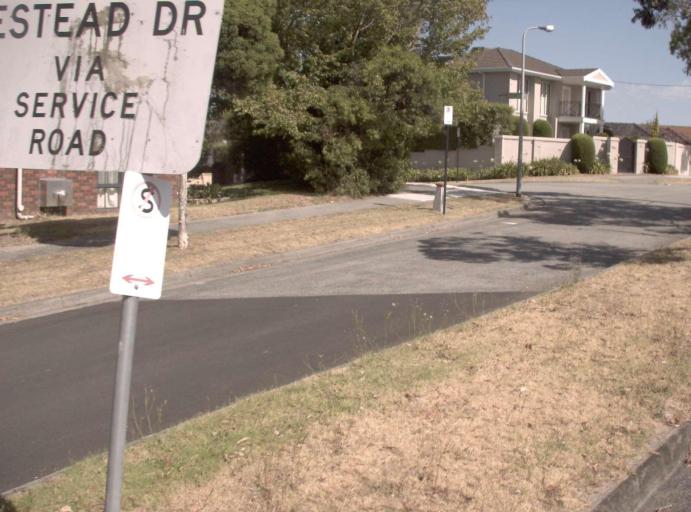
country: AU
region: Victoria
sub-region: Monash
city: Mulgrave
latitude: -37.9001
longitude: 145.1904
